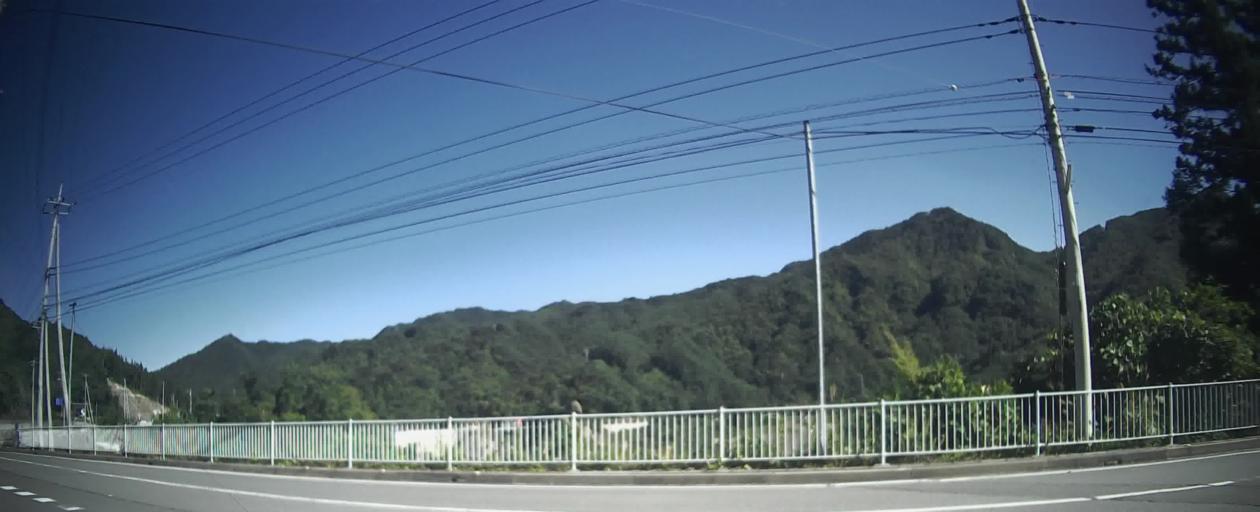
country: JP
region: Gunma
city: Nakanojomachi
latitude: 36.5567
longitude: 138.7057
